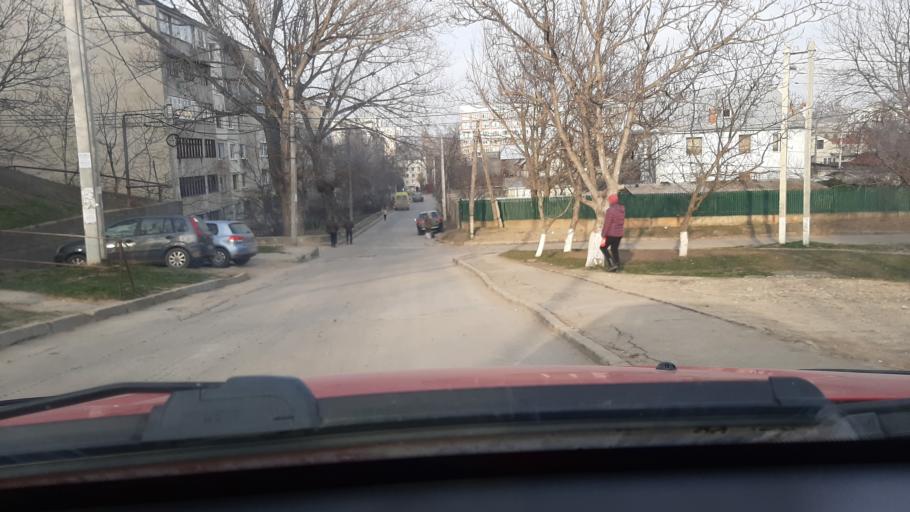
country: MD
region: Chisinau
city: Vatra
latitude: 47.0404
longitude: 28.7899
